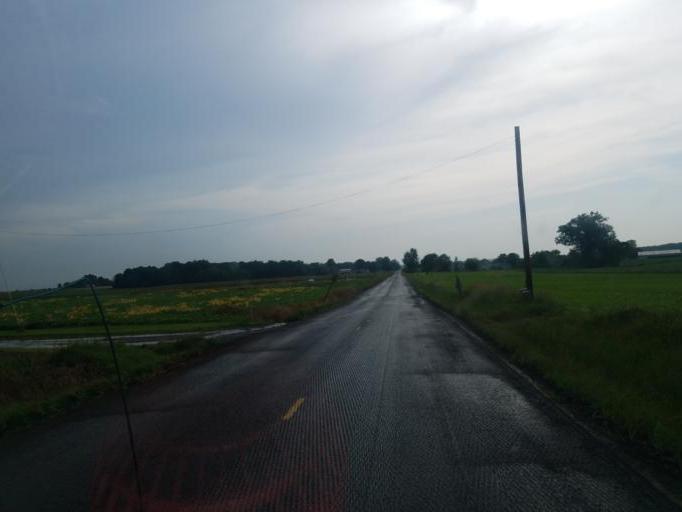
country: US
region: Ohio
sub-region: Wayne County
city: West Salem
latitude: 40.9240
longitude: -82.0691
